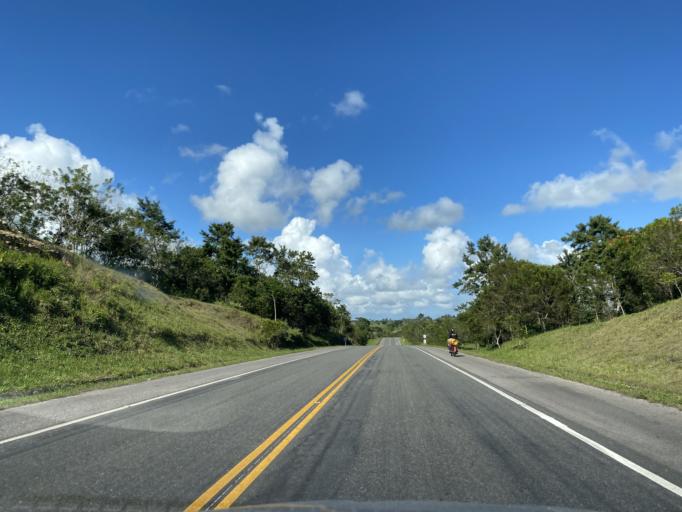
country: DO
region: Monte Plata
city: Majagual
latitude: 19.0182
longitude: -69.8228
